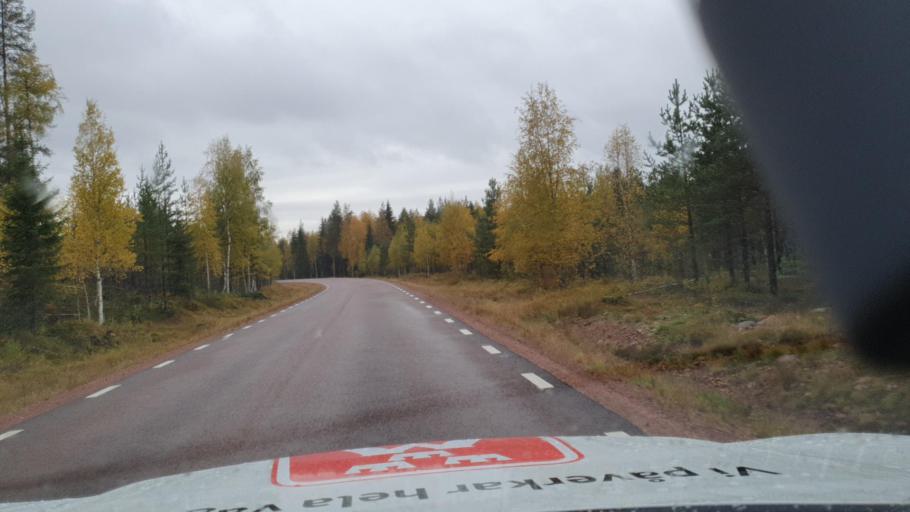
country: SE
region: Dalarna
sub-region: Alvdalens Kommun
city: AElvdalen
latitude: 61.3944
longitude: 14.1222
